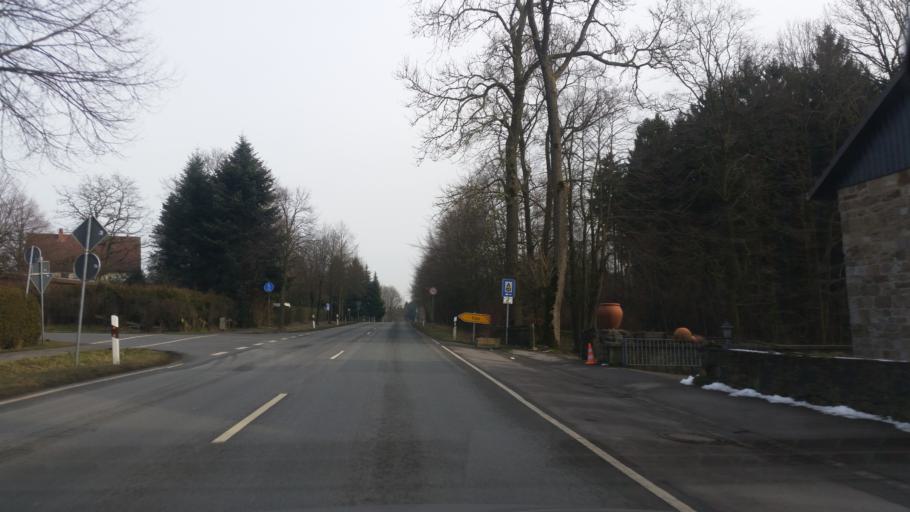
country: DE
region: North Rhine-Westphalia
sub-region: Regierungsbezirk Detmold
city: Barntrup
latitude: 52.0679
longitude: 9.1473
